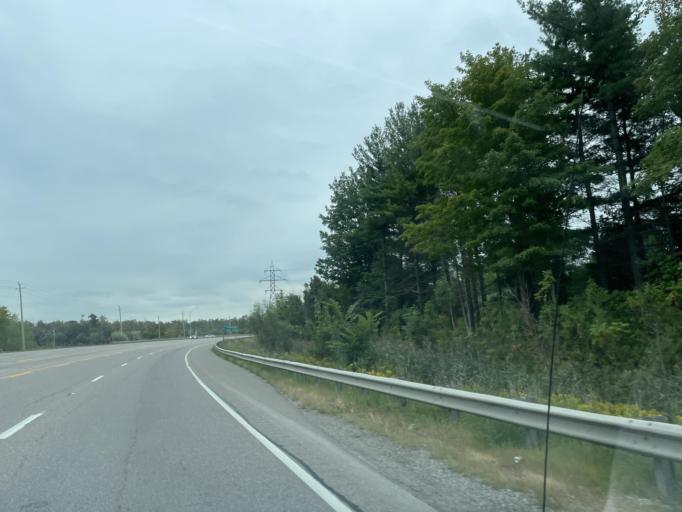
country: CA
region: Ontario
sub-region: Halton
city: Milton
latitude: 43.4097
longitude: -80.0506
